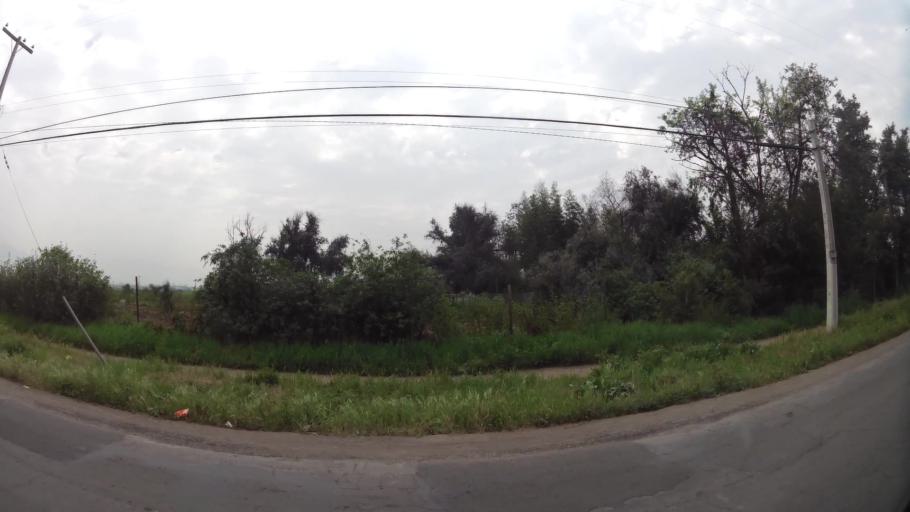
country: CL
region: Santiago Metropolitan
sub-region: Provincia de Chacabuco
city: Chicureo Abajo
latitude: -33.2097
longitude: -70.6855
